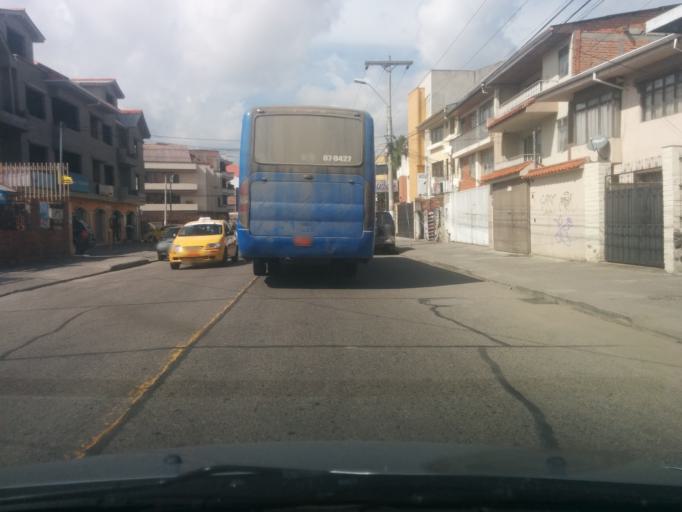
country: EC
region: Azuay
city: Cuenca
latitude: -2.9005
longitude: -78.9915
